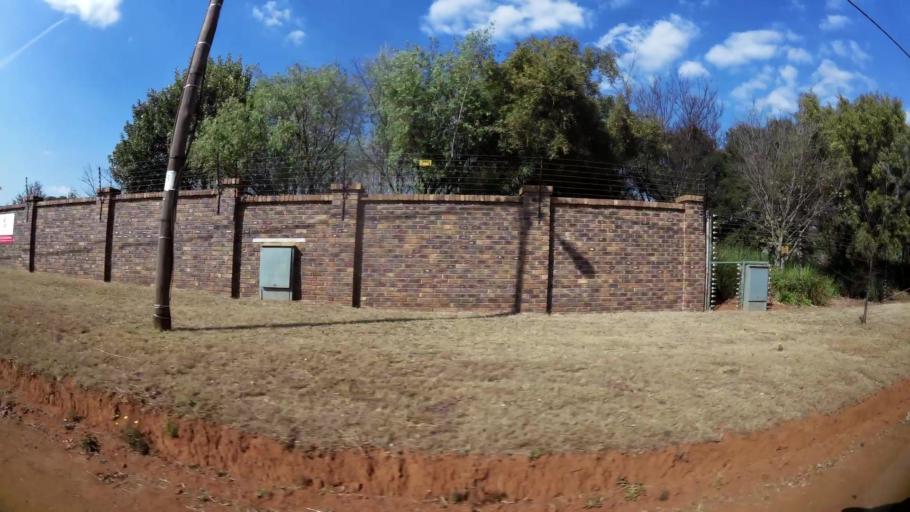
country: ZA
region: Gauteng
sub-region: Ekurhuleni Metropolitan Municipality
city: Benoni
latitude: -26.0821
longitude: 28.3272
